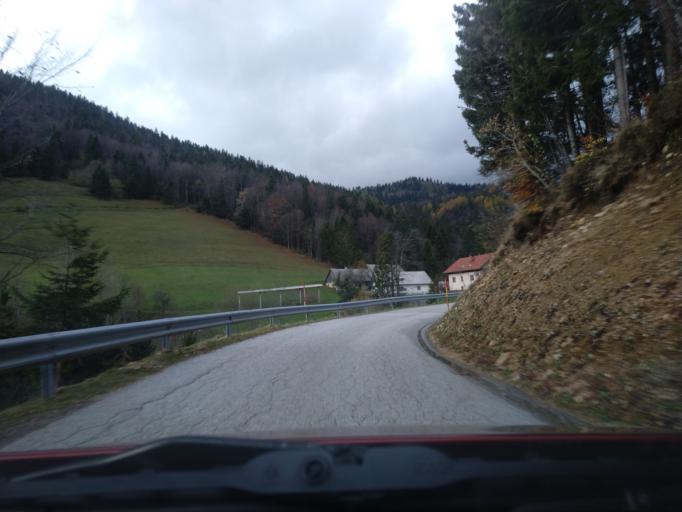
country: SI
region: Kamnik
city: Mekinje
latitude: 46.2820
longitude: 14.6894
